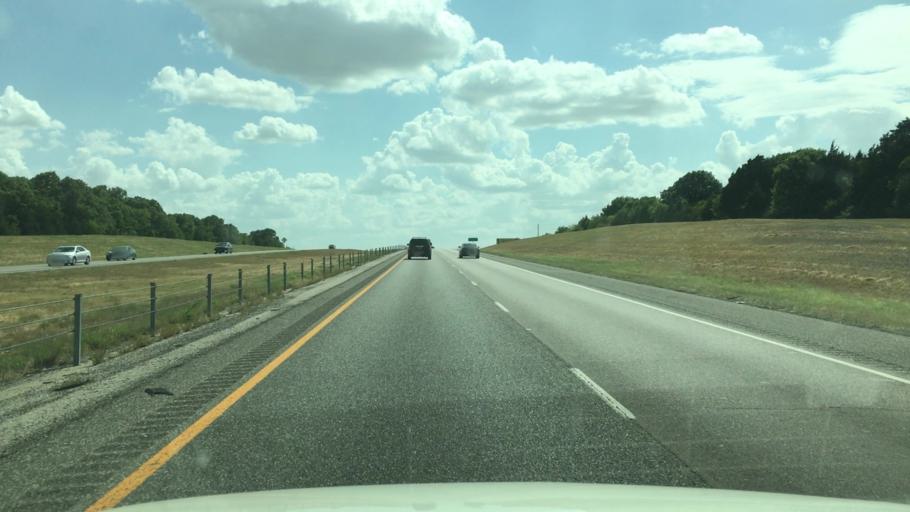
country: US
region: Texas
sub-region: Ellis County
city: Plum Grove
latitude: 32.0937
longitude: -97.0274
